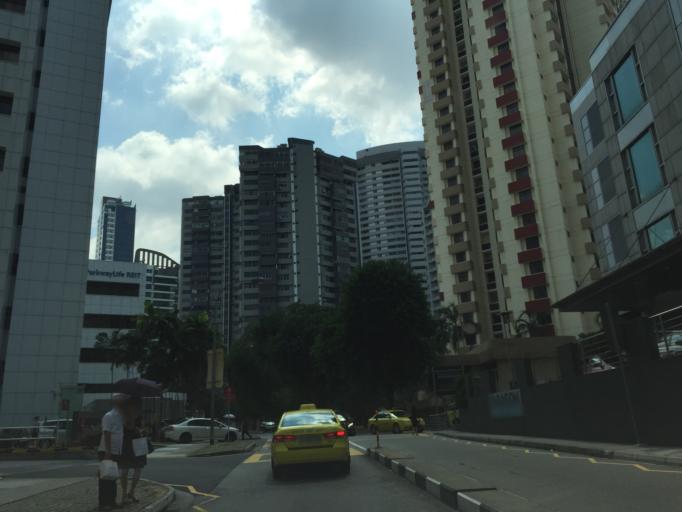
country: SG
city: Singapore
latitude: 1.3045
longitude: 103.8356
